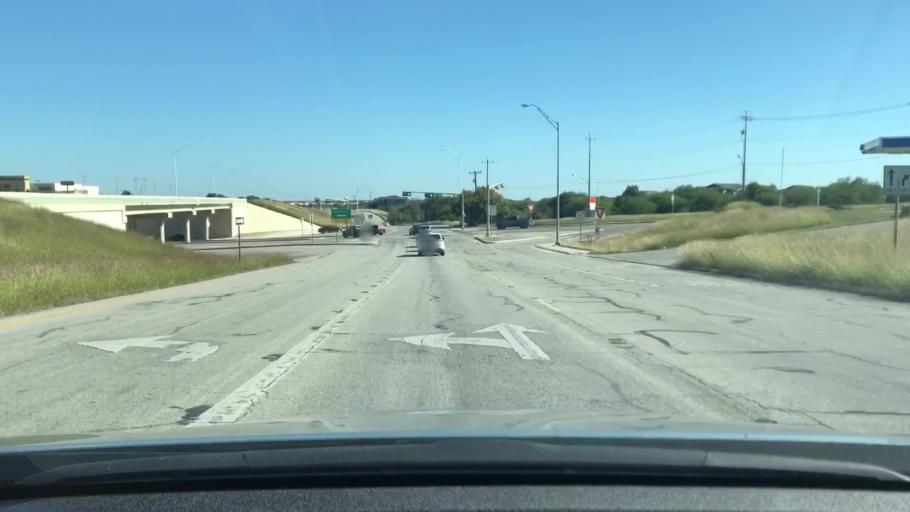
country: US
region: Texas
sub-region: Bexar County
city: Universal City
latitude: 29.5470
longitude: -98.3169
